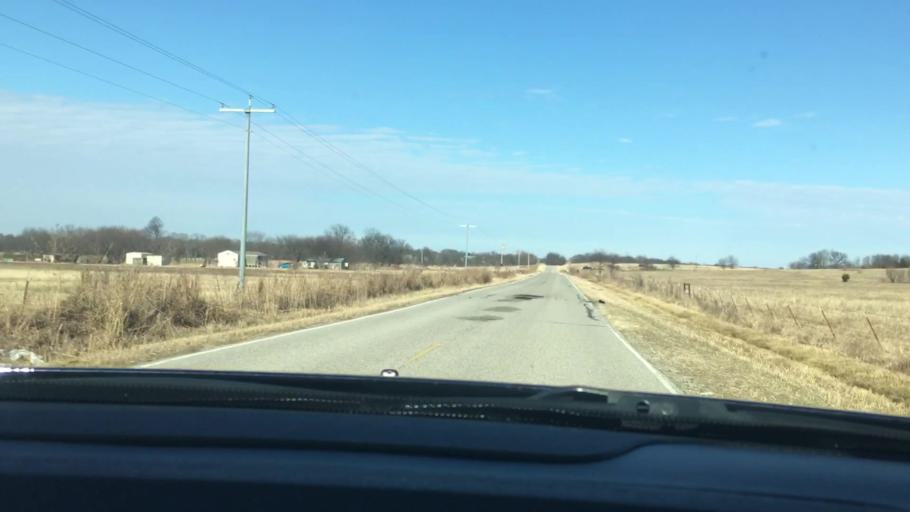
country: US
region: Oklahoma
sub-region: Garvin County
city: Wynnewood
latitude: 34.7141
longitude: -97.1254
